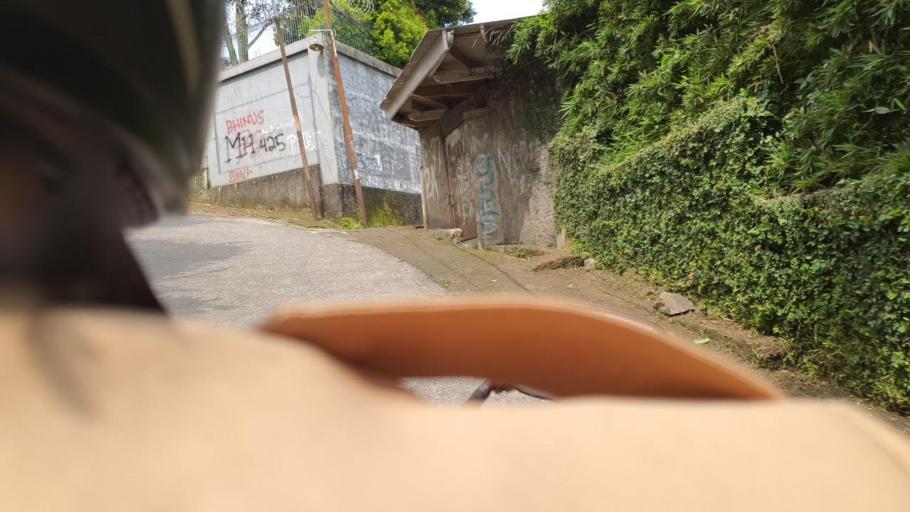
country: ID
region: West Java
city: Caringin
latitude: -6.6496
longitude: 106.8869
